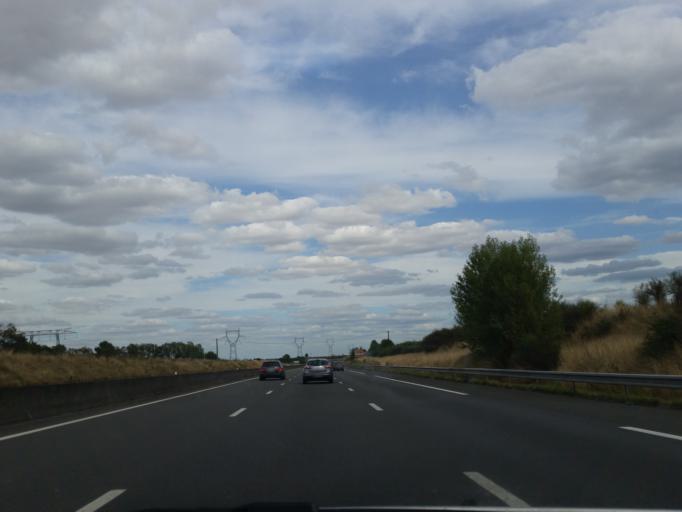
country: FR
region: Centre
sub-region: Departement du Loir-et-Cher
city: Herbault
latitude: 47.6110
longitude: 1.1383
